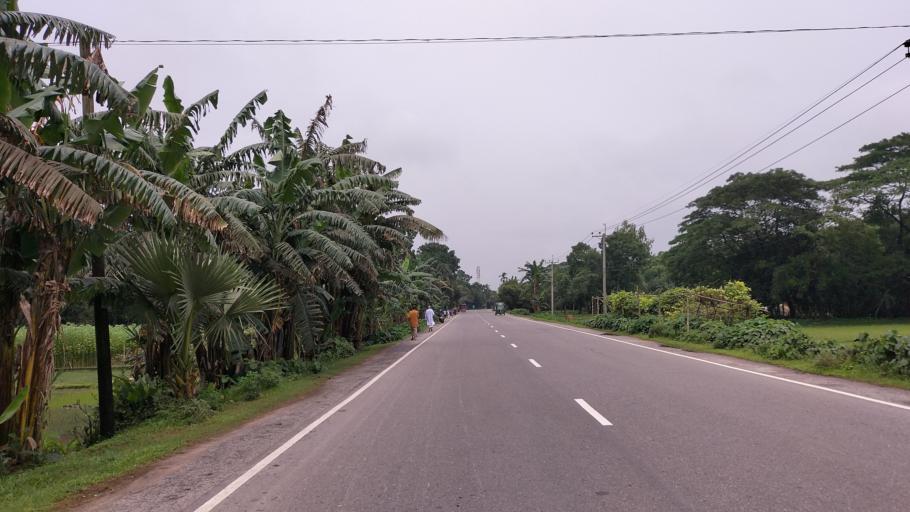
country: BD
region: Dhaka
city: Netrakona
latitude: 24.8503
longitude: 90.6367
